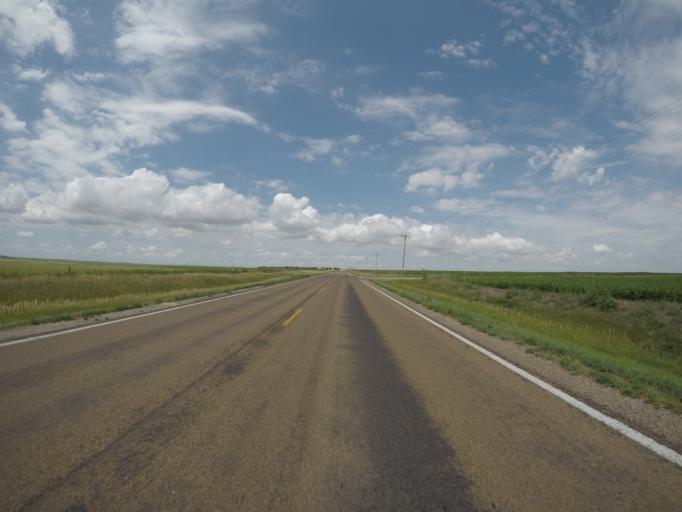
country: US
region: Kansas
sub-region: Rawlins County
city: Atwood
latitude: 39.8494
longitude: -101.0467
